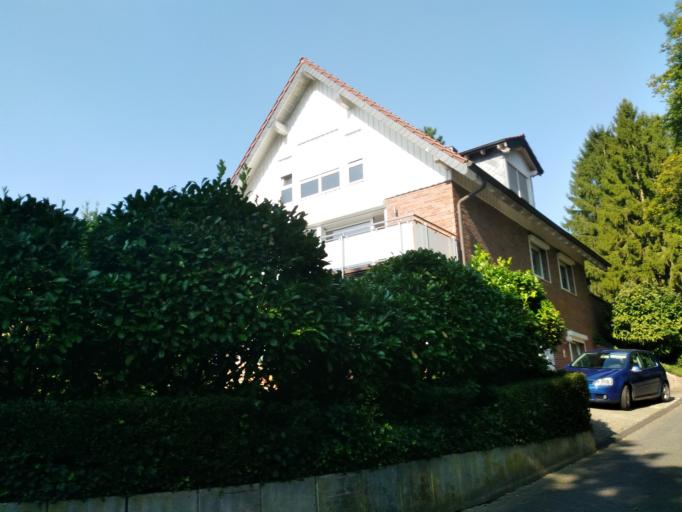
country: DE
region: North Rhine-Westphalia
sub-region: Regierungsbezirk Koln
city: Bad Honnef
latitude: 50.6556
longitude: 7.2238
